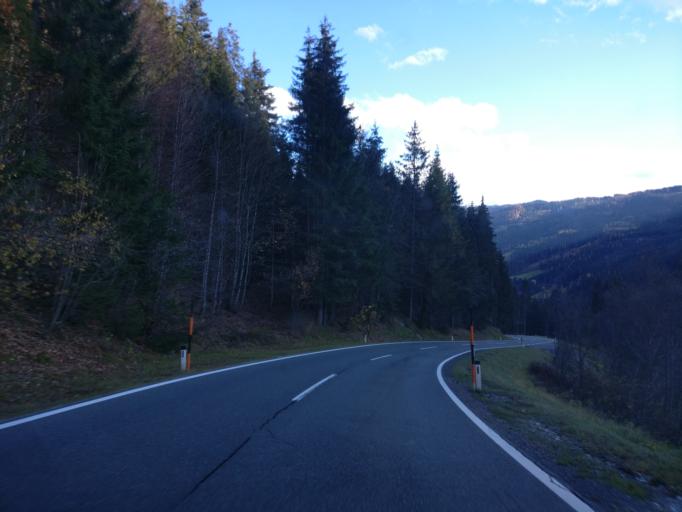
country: AT
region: Salzburg
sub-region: Politischer Bezirk Sankt Johann im Pongau
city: Muhlbach am Hochkonig
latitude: 47.3898
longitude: 13.0995
